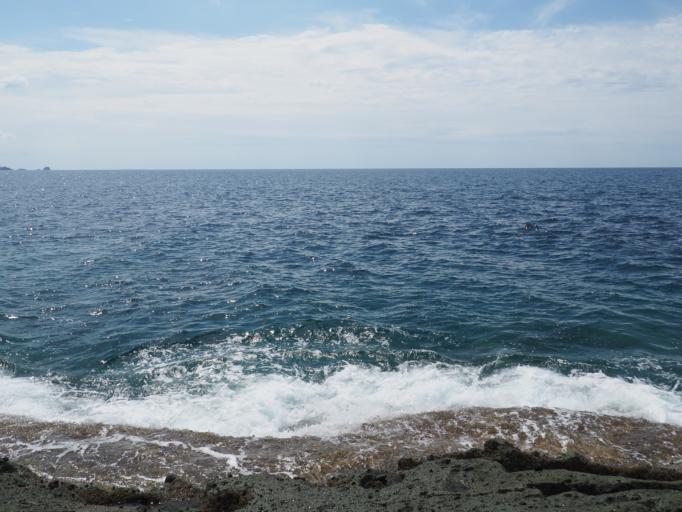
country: IT
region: Sardinia
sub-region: Provincia di Oristano
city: Bosa
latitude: 40.2941
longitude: 8.4689
